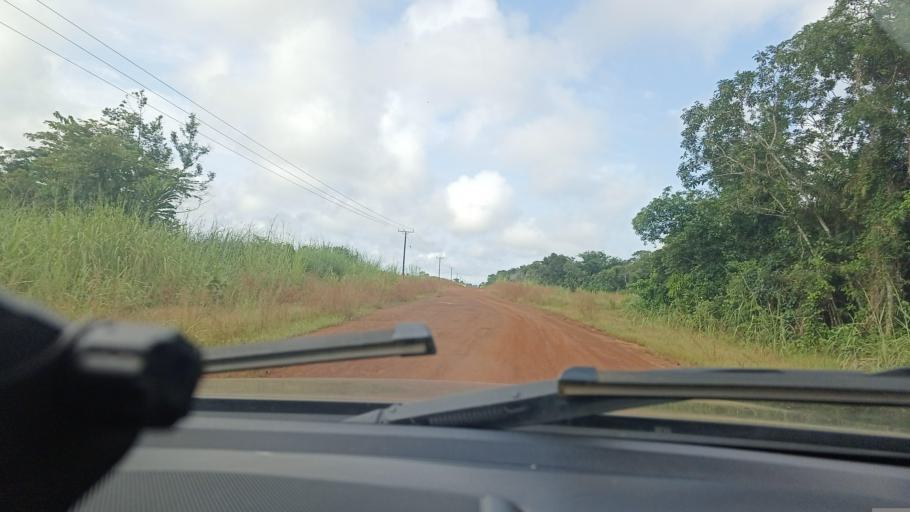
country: LR
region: Grand Cape Mount
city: Robertsport
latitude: 6.6987
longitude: -11.0976
